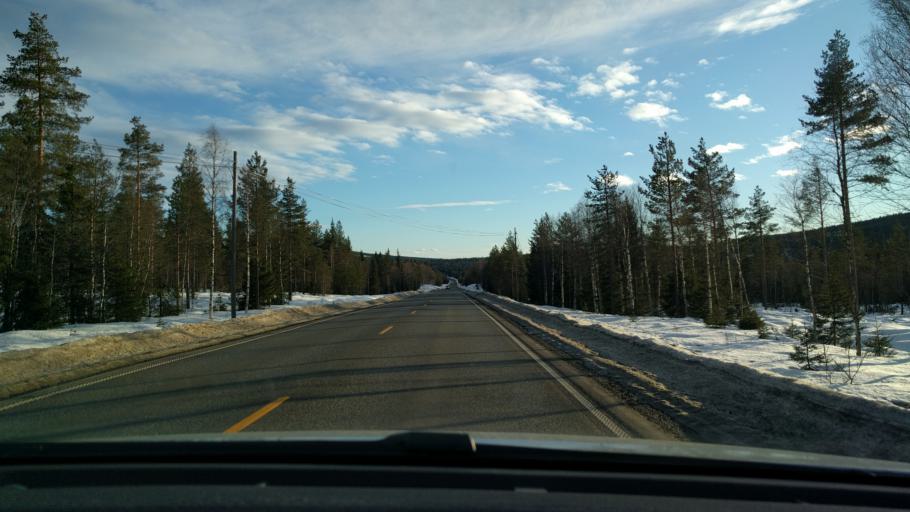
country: NO
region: Hedmark
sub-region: Elverum
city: Elverum
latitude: 61.0404
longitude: 11.8719
